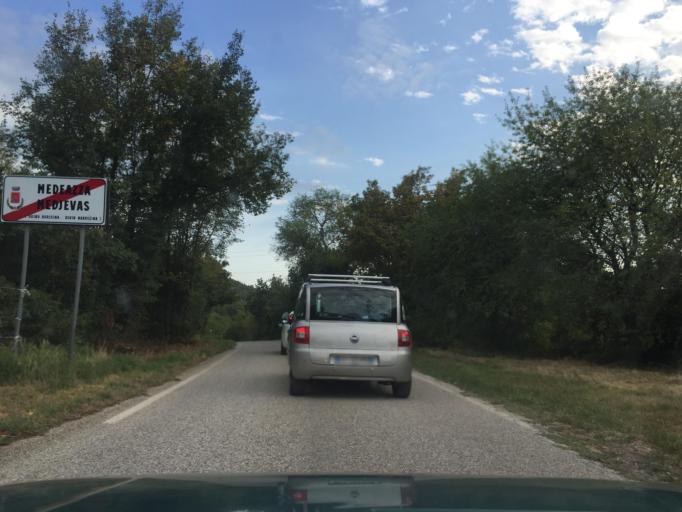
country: IT
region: Friuli Venezia Giulia
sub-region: Provincia di Trieste
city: Duino
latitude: 45.7956
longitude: 13.6014
